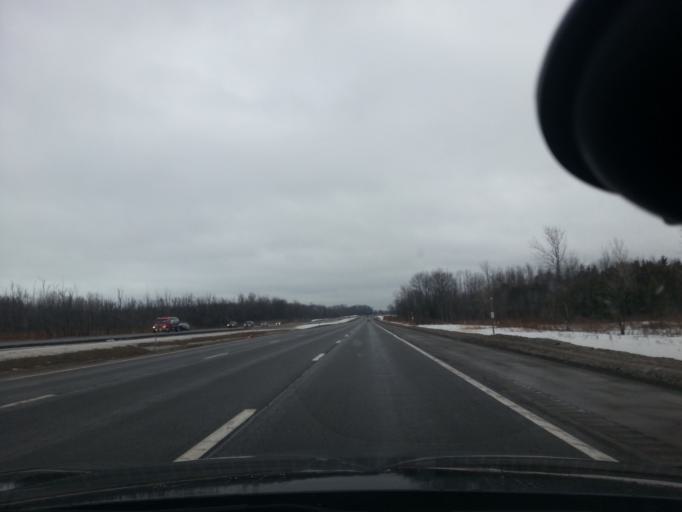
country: US
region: New York
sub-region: Oswego County
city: Central Square
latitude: 43.2651
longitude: -76.1314
